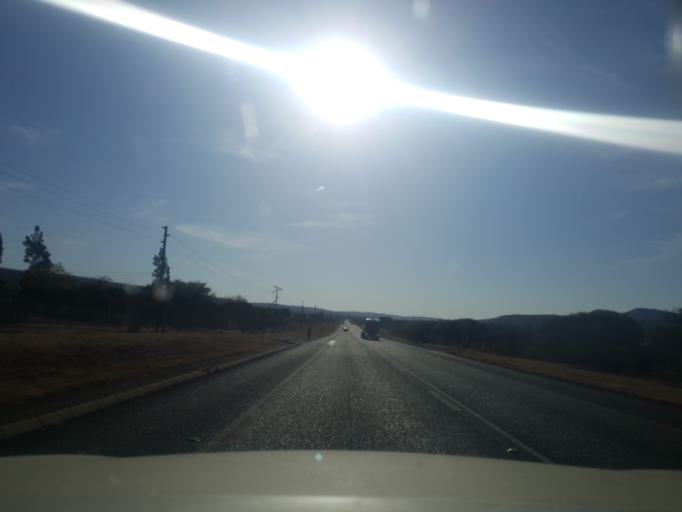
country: ZA
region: North-West
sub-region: Ngaka Modiri Molema District Municipality
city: Zeerust
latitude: -25.4401
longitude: 25.8487
